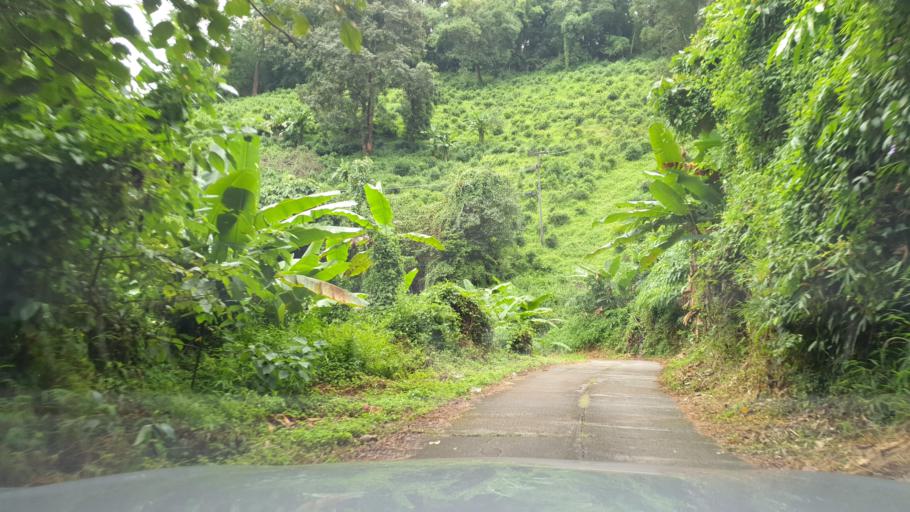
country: TH
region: Chiang Mai
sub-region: Amphoe Chiang Dao
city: Chiang Dao
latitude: 19.2718
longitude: 98.9334
